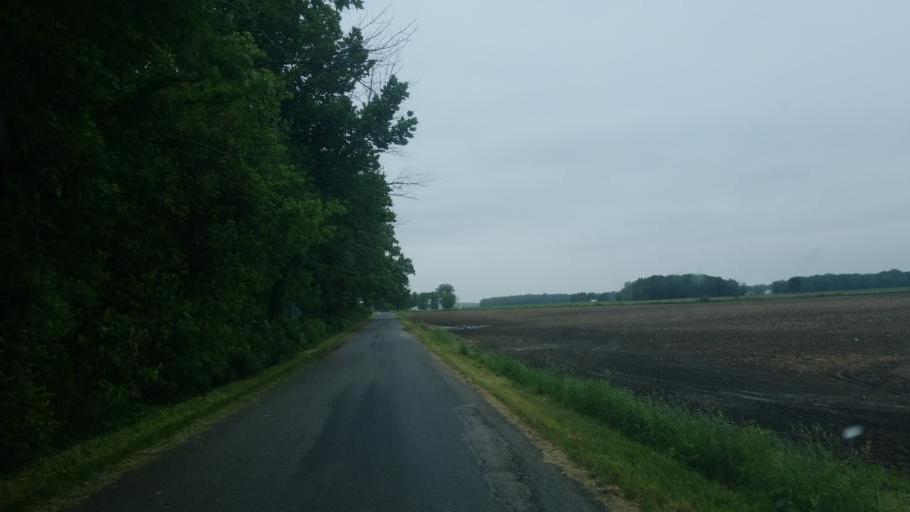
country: US
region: Indiana
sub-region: Marshall County
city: Bremen
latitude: 41.4936
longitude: -86.1196
